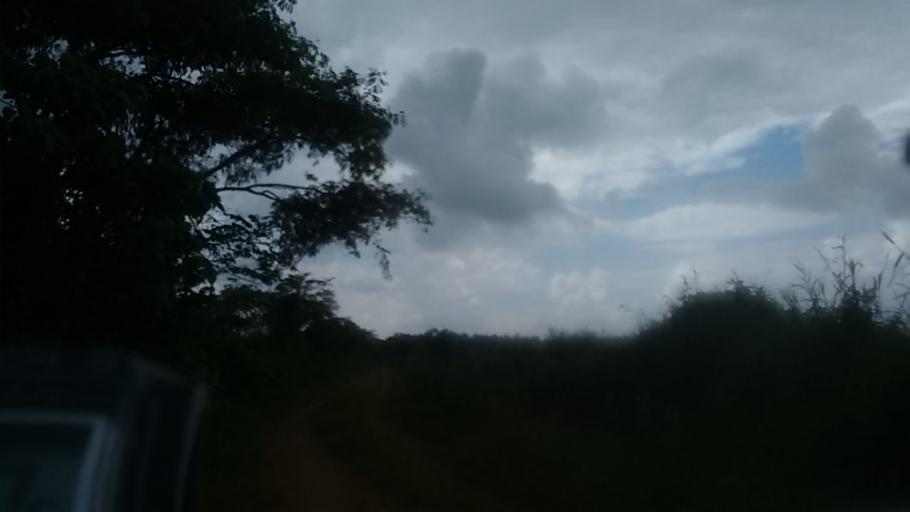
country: IN
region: Kerala
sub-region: Thrissur District
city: Trichur
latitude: 10.5311
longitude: 76.1655
